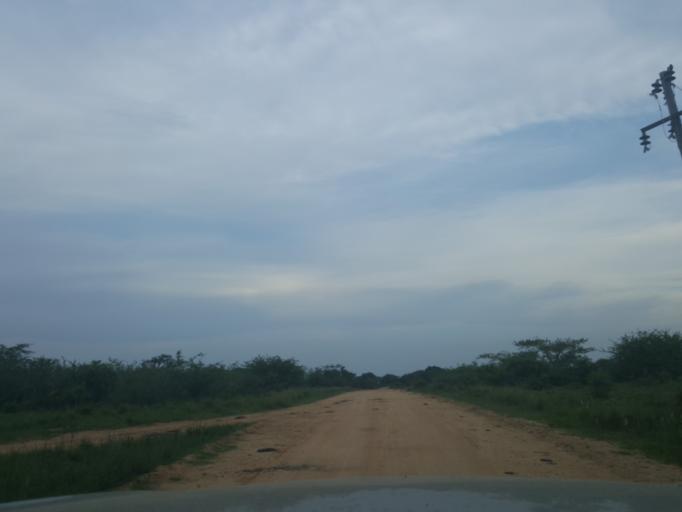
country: ZA
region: Limpopo
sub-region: Mopani District Municipality
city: Hoedspruit
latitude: -24.5903
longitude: 30.9462
